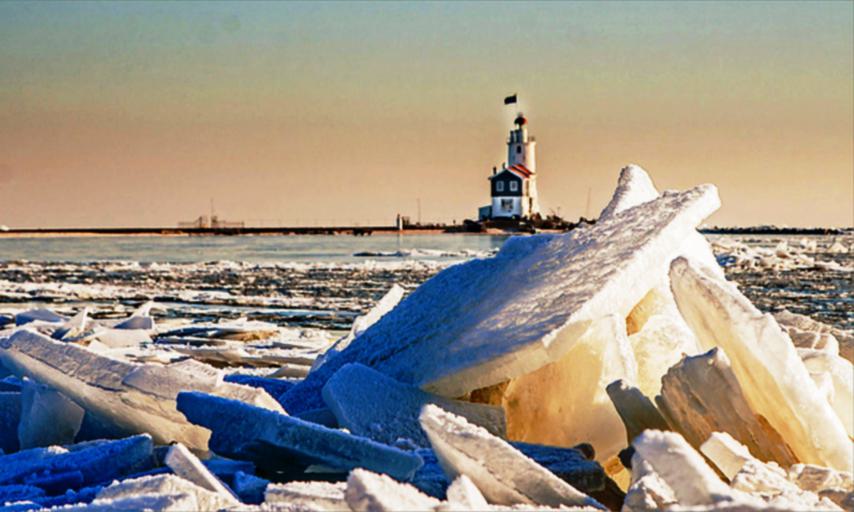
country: NL
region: Flevoland
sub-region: Gemeente Urk
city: Urk
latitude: 52.6625
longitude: 5.5925
